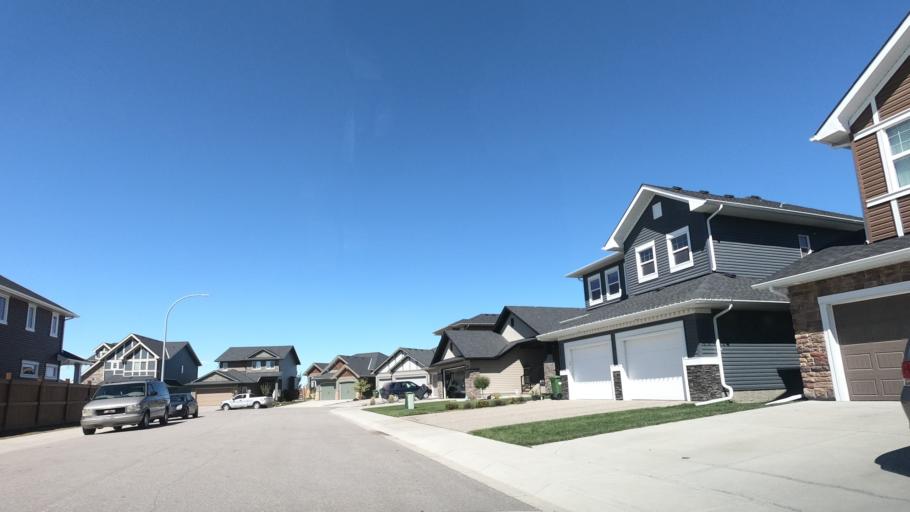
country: CA
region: Alberta
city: Airdrie
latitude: 51.2649
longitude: -113.9801
